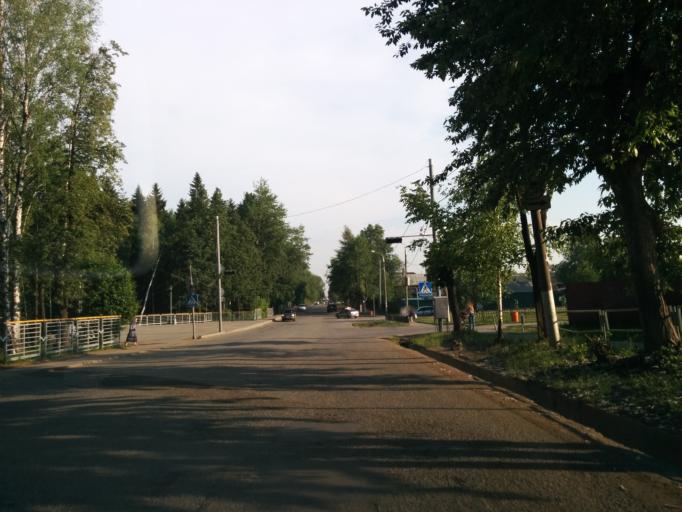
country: RU
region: Perm
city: Perm
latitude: 58.1135
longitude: 56.2968
